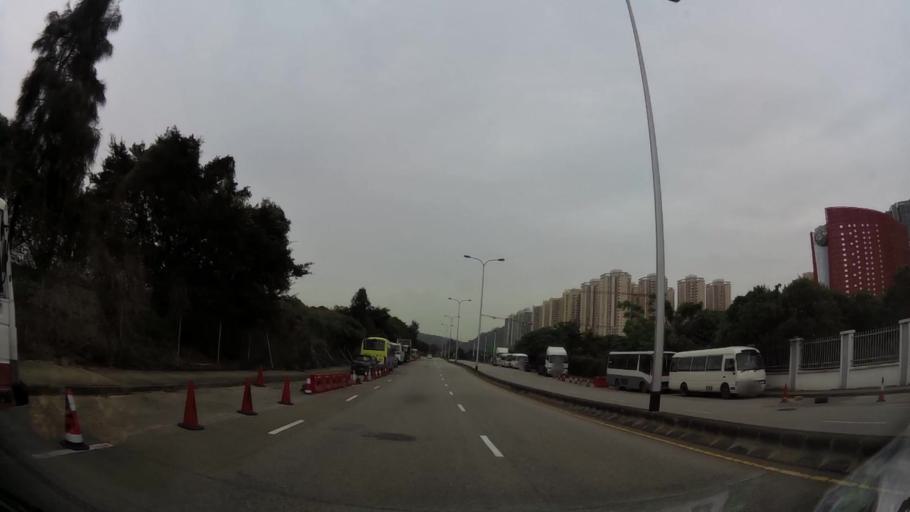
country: MO
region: Macau
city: Macau
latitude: 22.1318
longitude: 113.5568
